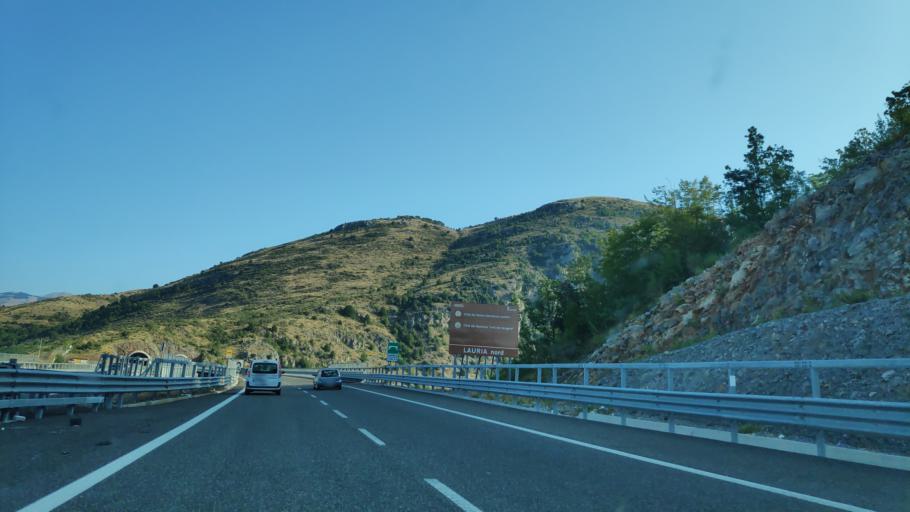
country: IT
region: Basilicate
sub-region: Provincia di Potenza
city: Lauria
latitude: 40.0335
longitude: 15.8745
